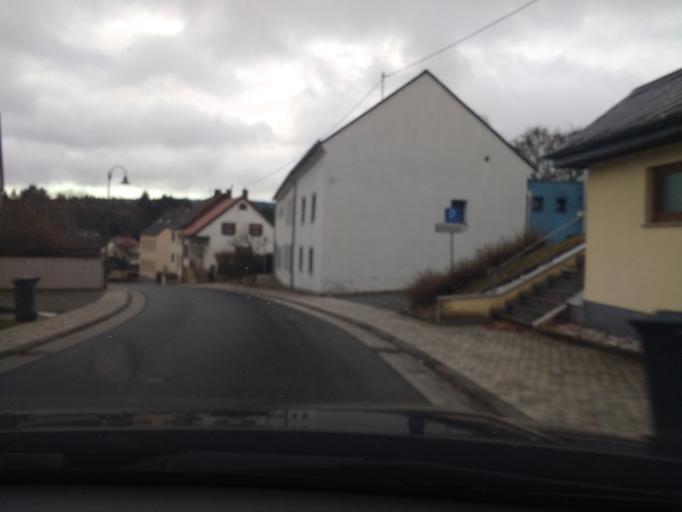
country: DE
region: Rheinland-Pfalz
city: Zusch
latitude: 49.6486
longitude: 7.0058
